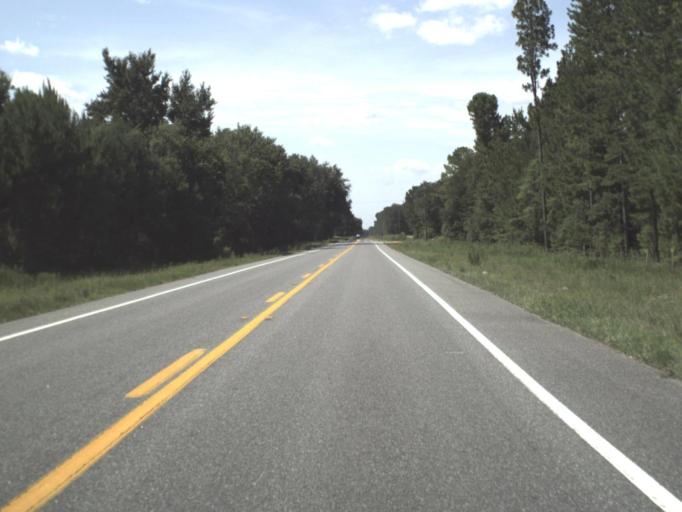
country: US
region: Florida
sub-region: Alachua County
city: High Springs
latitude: 29.8321
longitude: -82.7416
